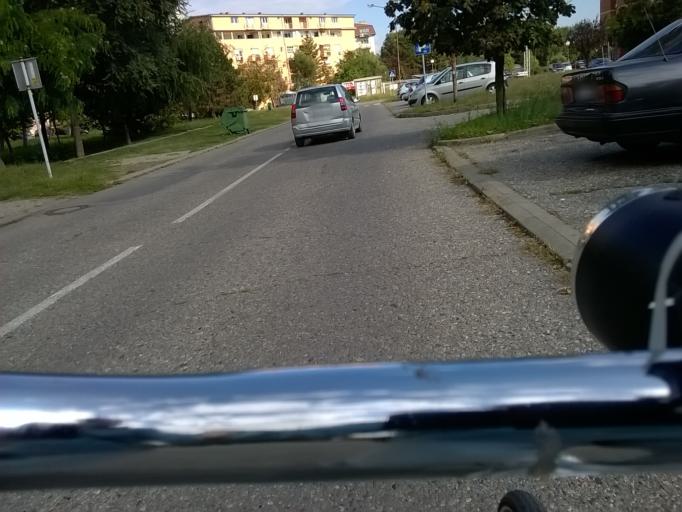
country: RS
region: Autonomna Pokrajina Vojvodina
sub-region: Juznobanatski Okrug
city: Pancevo
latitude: 44.8636
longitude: 20.6424
